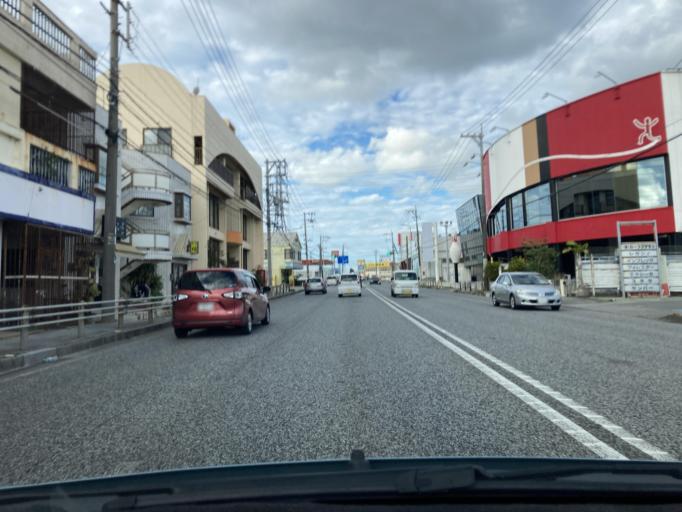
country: JP
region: Okinawa
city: Ishikawa
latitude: 26.3842
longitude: 127.8277
